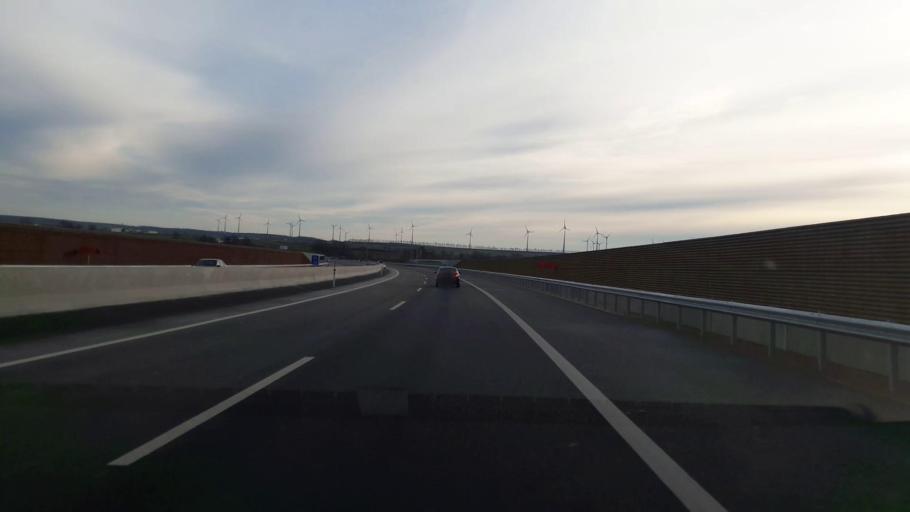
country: AT
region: Lower Austria
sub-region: Politischer Bezirk Mistelbach
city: Wilfersdorf
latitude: 48.5782
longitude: 16.6242
